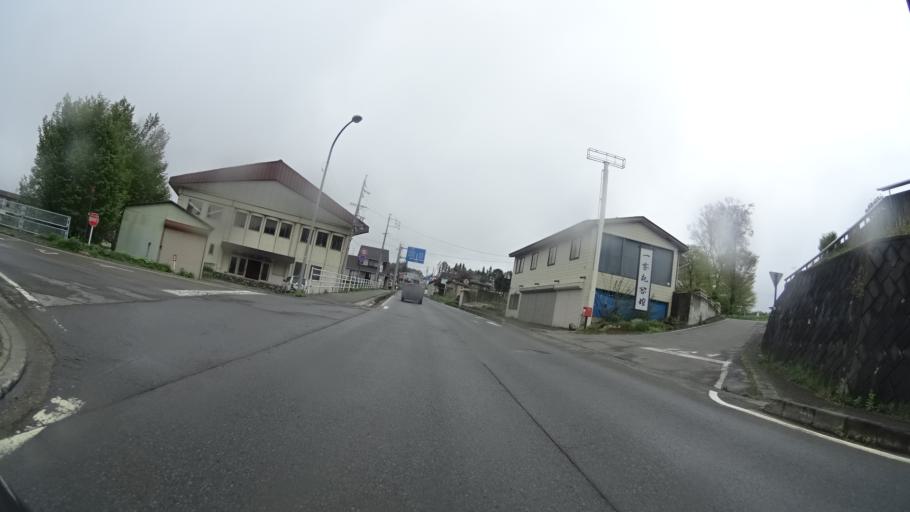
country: JP
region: Nagano
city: Nagano-shi
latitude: 36.8091
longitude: 138.2003
